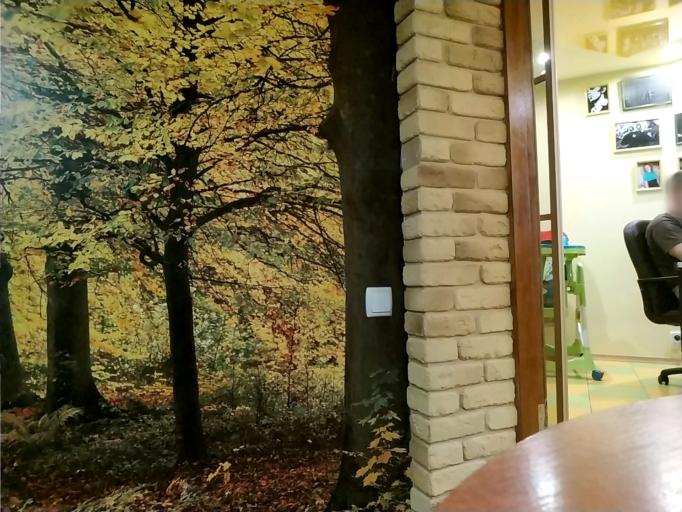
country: RU
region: Tverskaya
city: Zapadnaya Dvina
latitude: 56.3323
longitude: 31.8829
